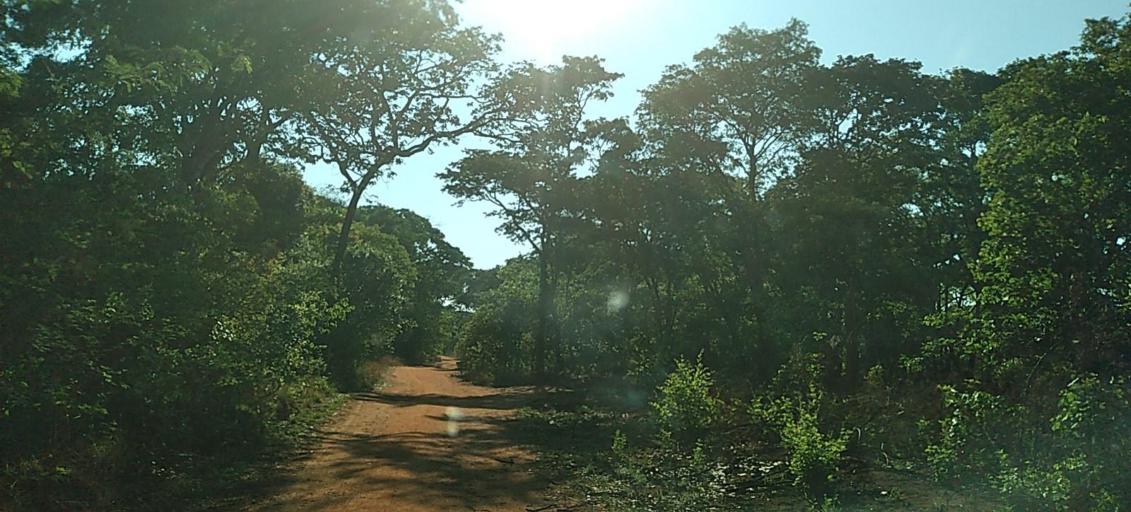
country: ZM
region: Copperbelt
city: Luanshya
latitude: -13.4588
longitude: 28.8278
